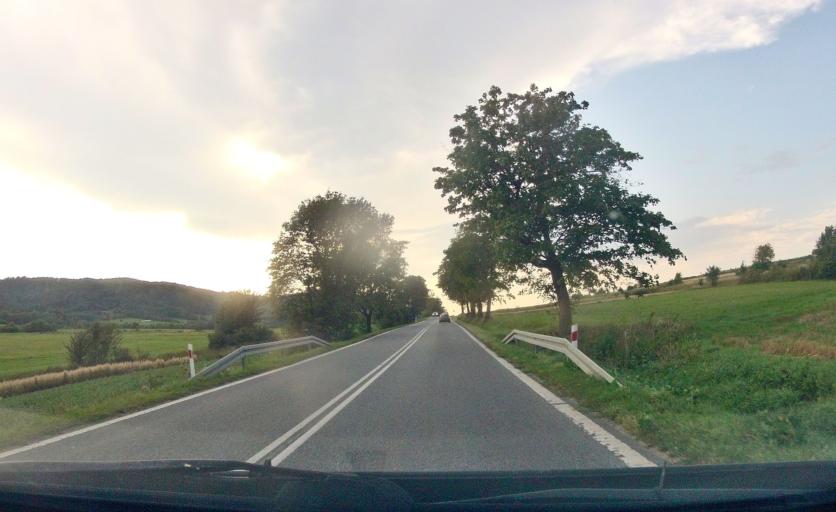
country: PL
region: Subcarpathian Voivodeship
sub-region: Powiat jasielski
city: Nowy Zmigrod
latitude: 49.5661
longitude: 21.5861
